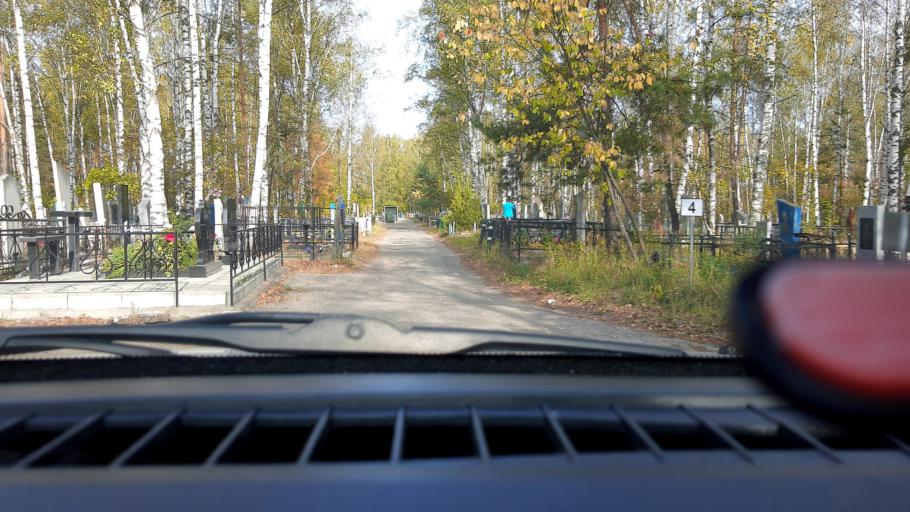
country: RU
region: Nizjnij Novgorod
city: Gorbatovka
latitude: 56.3566
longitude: 43.7838
